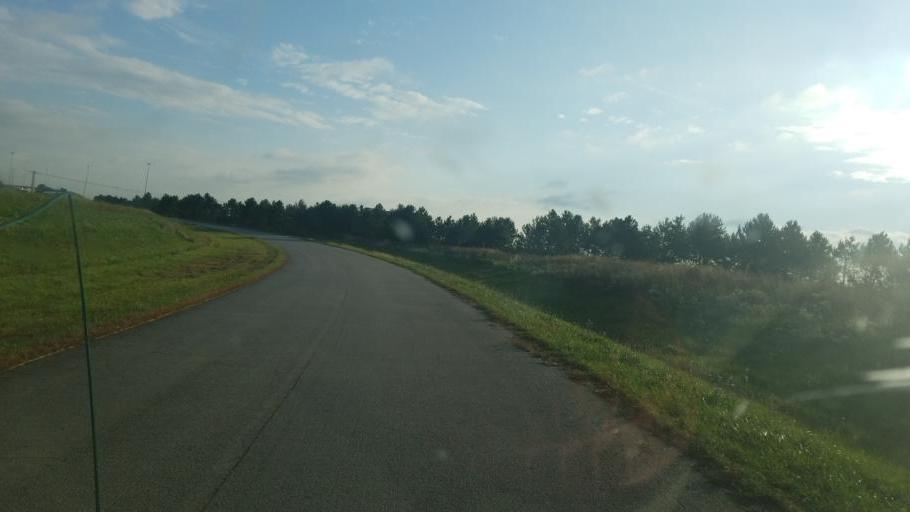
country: US
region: Ohio
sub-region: Wyandot County
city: Upper Sandusky
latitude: 40.8481
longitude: -83.3267
